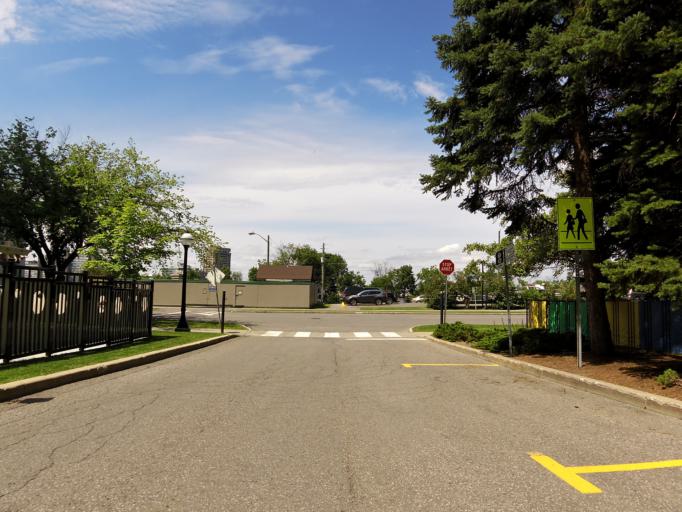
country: CA
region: Ontario
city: Ottawa
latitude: 45.4217
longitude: -75.7036
